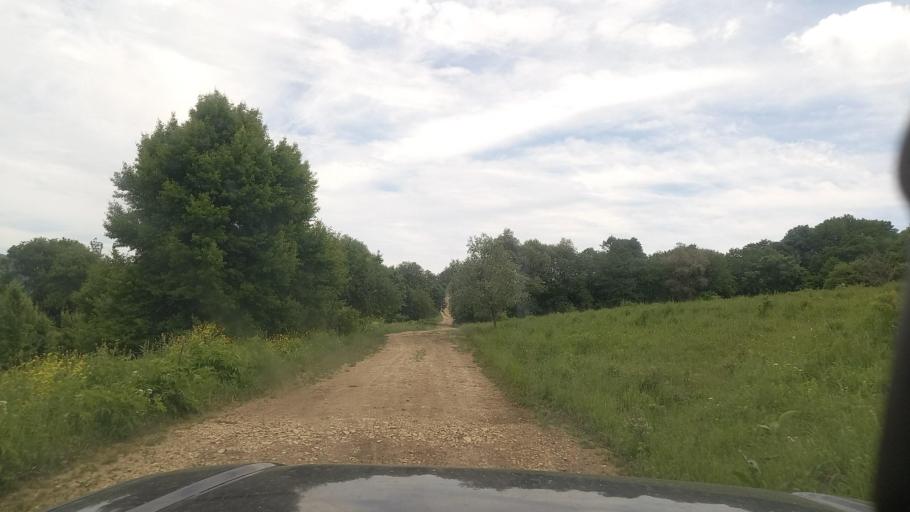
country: RU
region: Karachayevo-Cherkesiya
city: Pregradnaya
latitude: 44.0887
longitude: 41.1879
